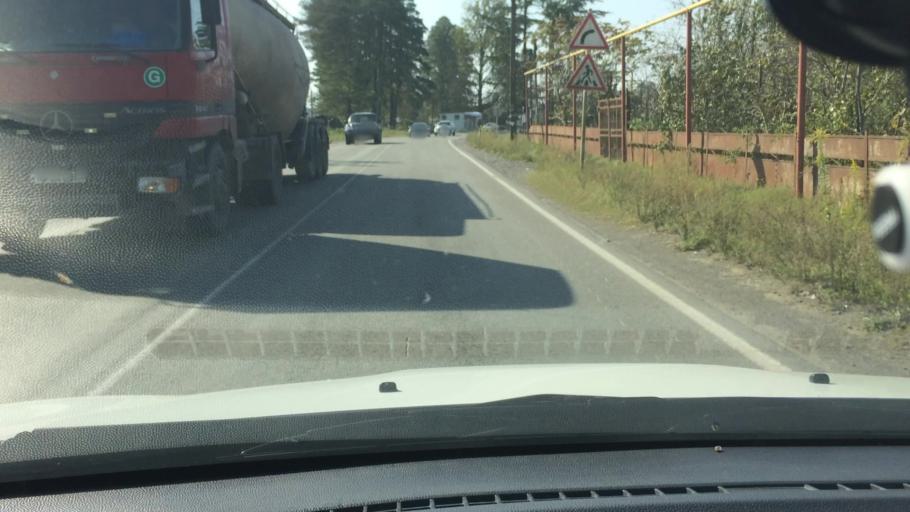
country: GE
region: Guria
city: Urek'i
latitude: 42.0444
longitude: 41.8140
